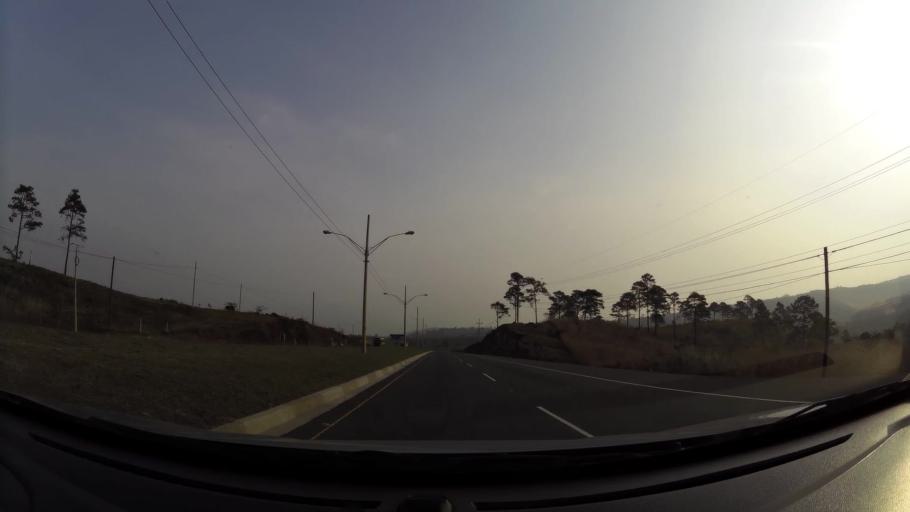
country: HN
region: Francisco Morazan
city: Tamara
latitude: 14.1781
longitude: -87.3116
